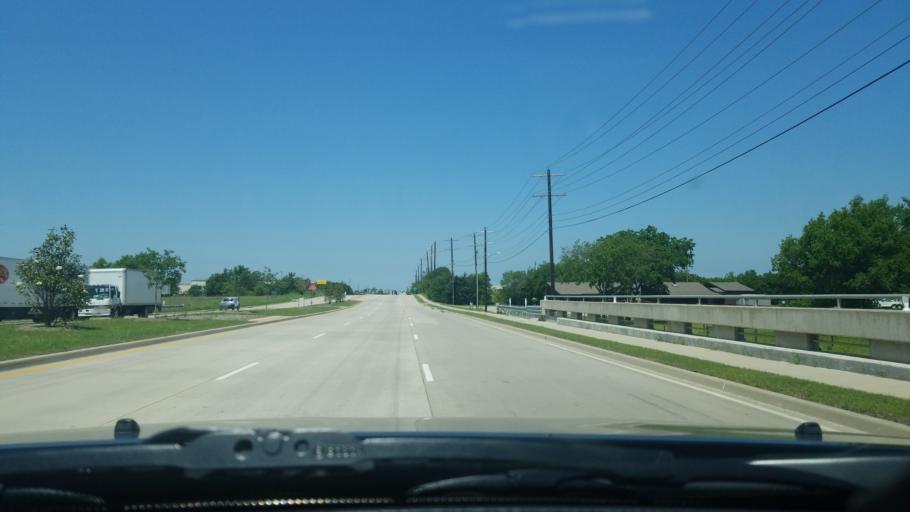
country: US
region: Texas
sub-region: Denton County
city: Krum
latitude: 33.2307
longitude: -97.1907
